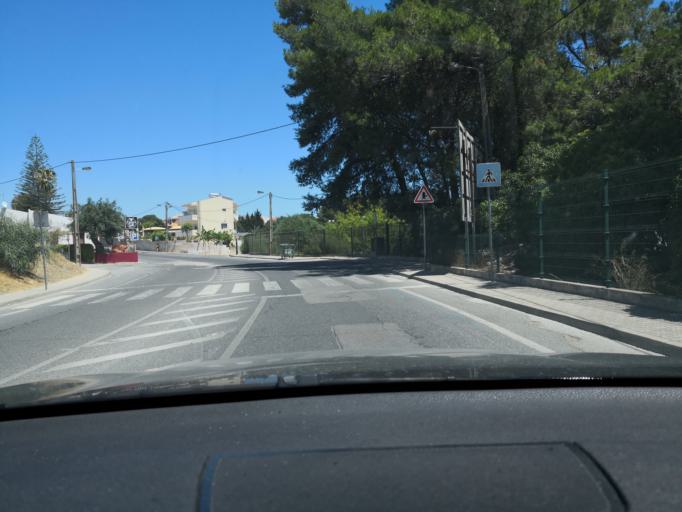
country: PT
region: Faro
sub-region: Albufeira
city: Albufeira
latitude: 37.0993
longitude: -8.2172
